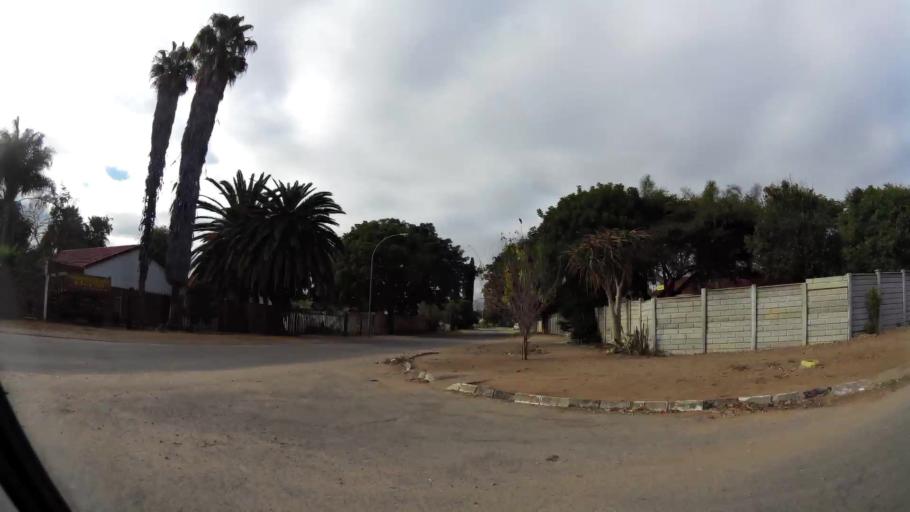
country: ZA
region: Limpopo
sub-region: Capricorn District Municipality
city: Polokwane
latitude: -23.9162
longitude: 29.4459
